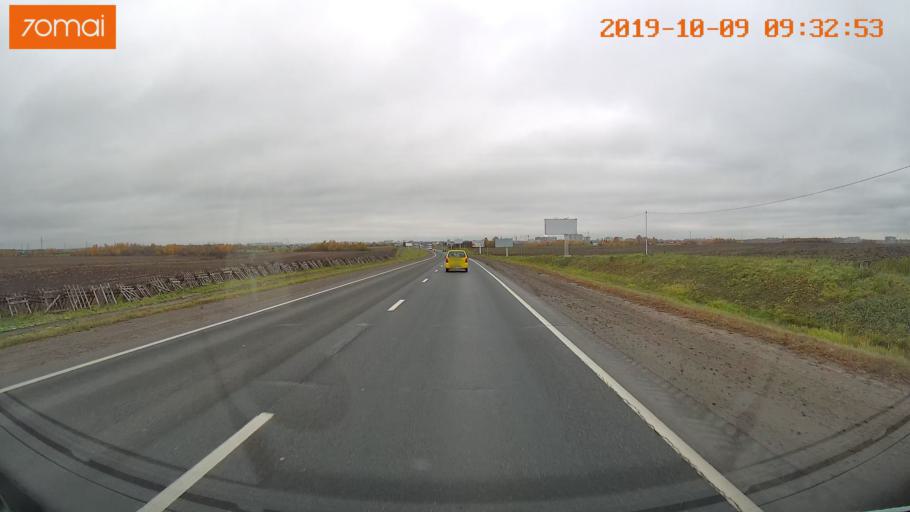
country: RU
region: Vologda
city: Vologda
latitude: 59.1636
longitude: 39.9224
